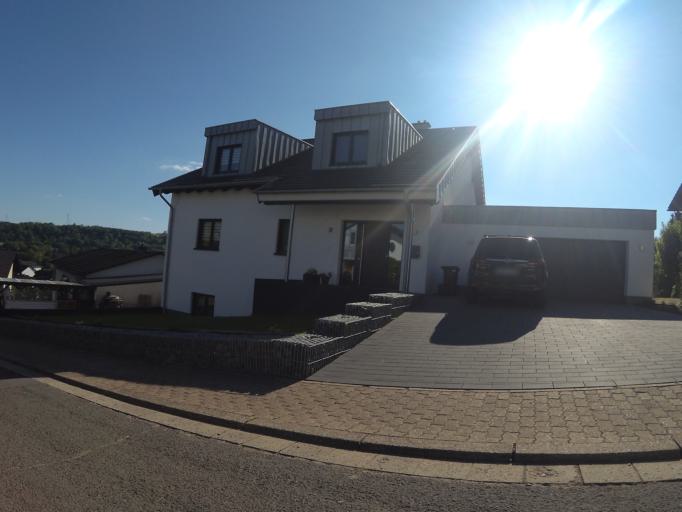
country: DE
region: Saarland
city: Britten
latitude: 49.4776
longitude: 6.6738
